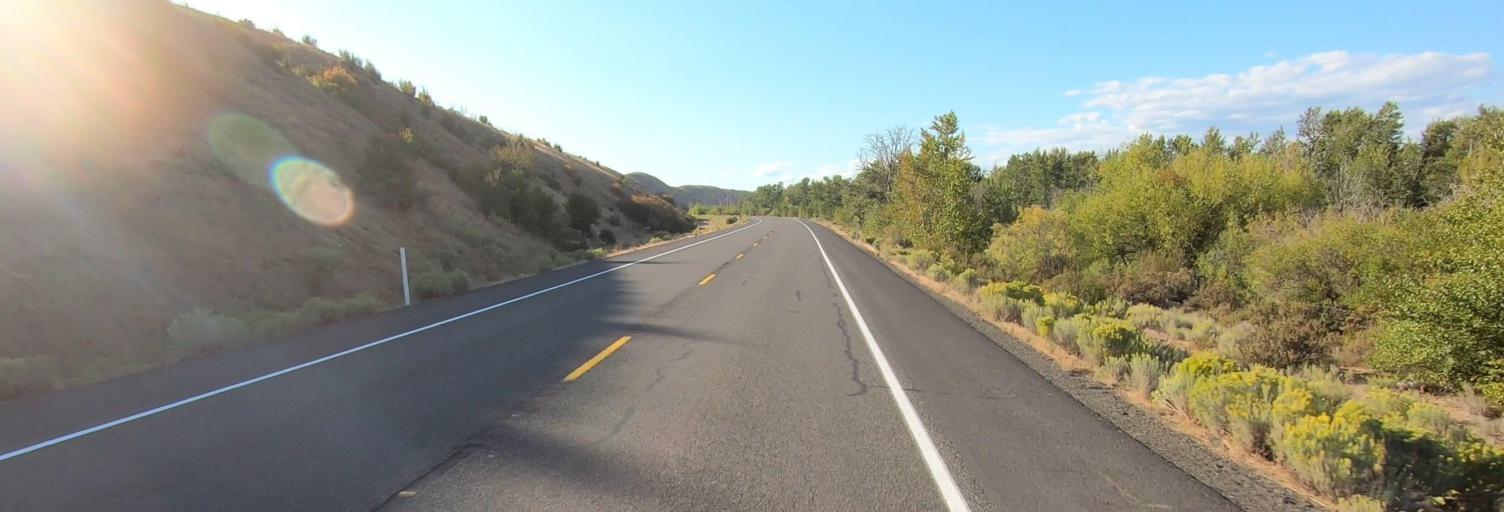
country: US
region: Washington
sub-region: Kittitas County
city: Ellensburg
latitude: 47.0826
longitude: -120.6413
